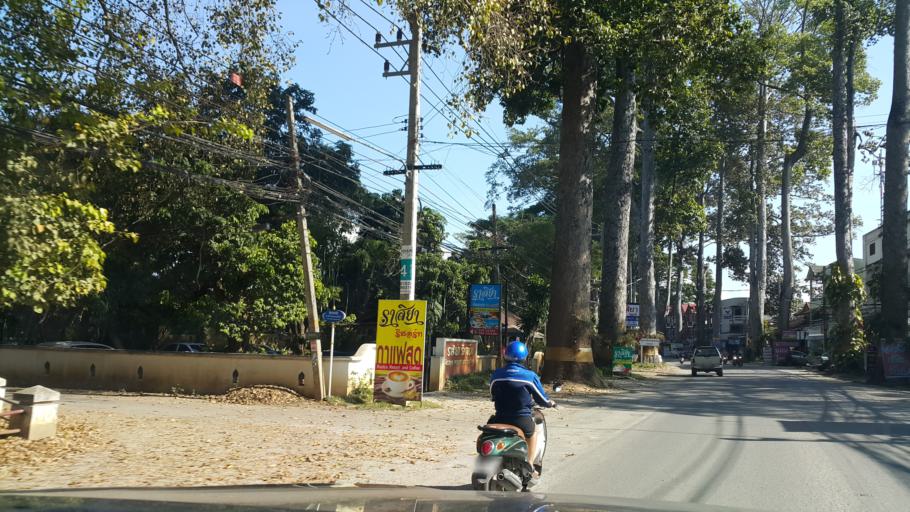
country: TH
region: Chiang Mai
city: Saraphi
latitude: 18.7346
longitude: 99.0168
